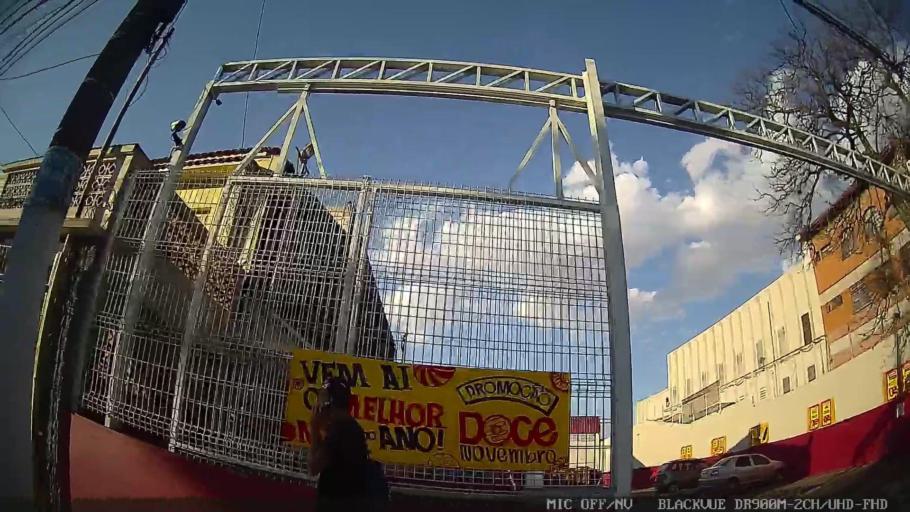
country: BR
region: Sao Paulo
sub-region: Sao Caetano Do Sul
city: Sao Caetano do Sul
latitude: -23.5776
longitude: -46.5474
